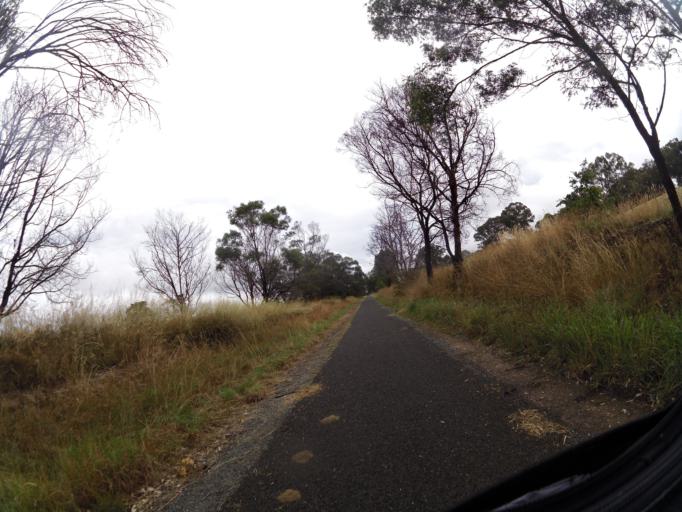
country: AU
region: Victoria
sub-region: East Gippsland
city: Bairnsdale
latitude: -37.8189
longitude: 147.7240
